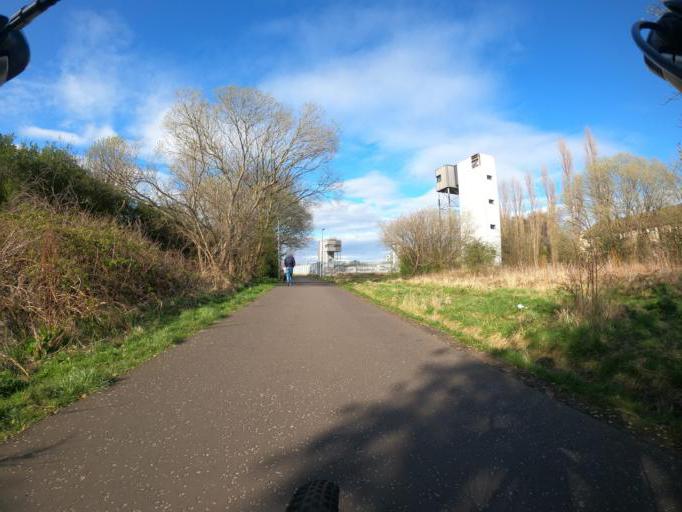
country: GB
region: Scotland
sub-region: Edinburgh
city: Edinburgh
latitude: 55.9660
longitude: -3.2407
